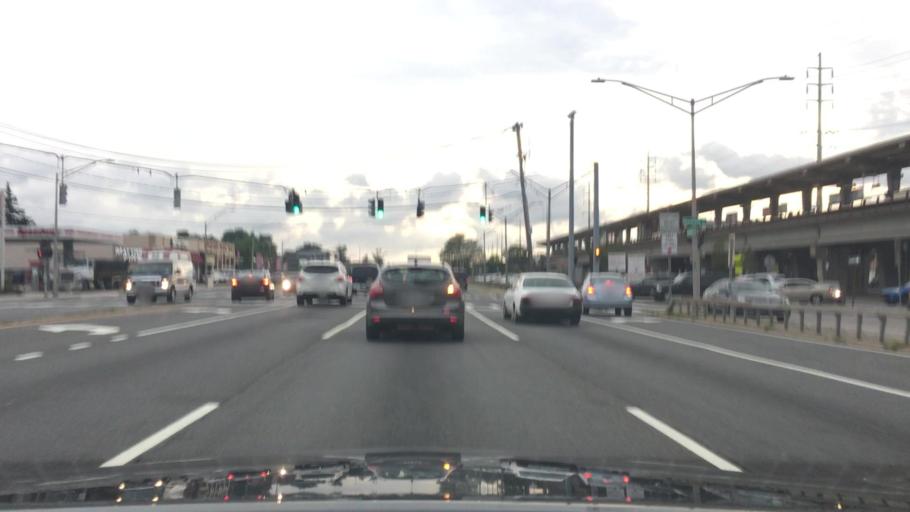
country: US
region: New York
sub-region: Nassau County
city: Merrick
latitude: 40.6638
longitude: -73.5490
